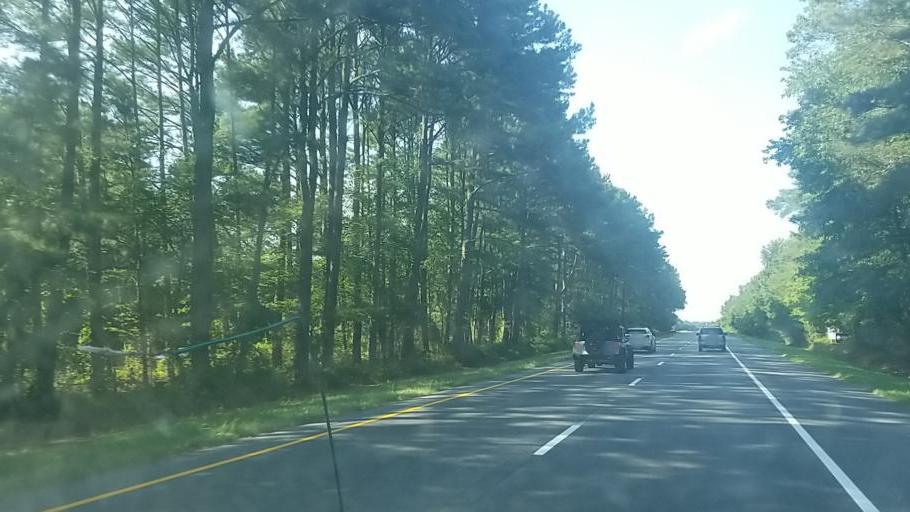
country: US
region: Maryland
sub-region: Worcester County
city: Berlin
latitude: 38.3508
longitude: -75.2145
